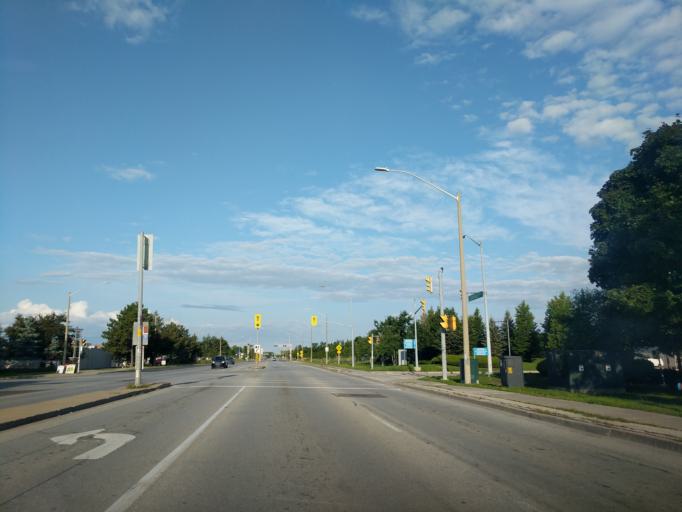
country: CA
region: Ontario
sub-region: York
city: Richmond Hill
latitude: 43.8920
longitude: -79.4309
